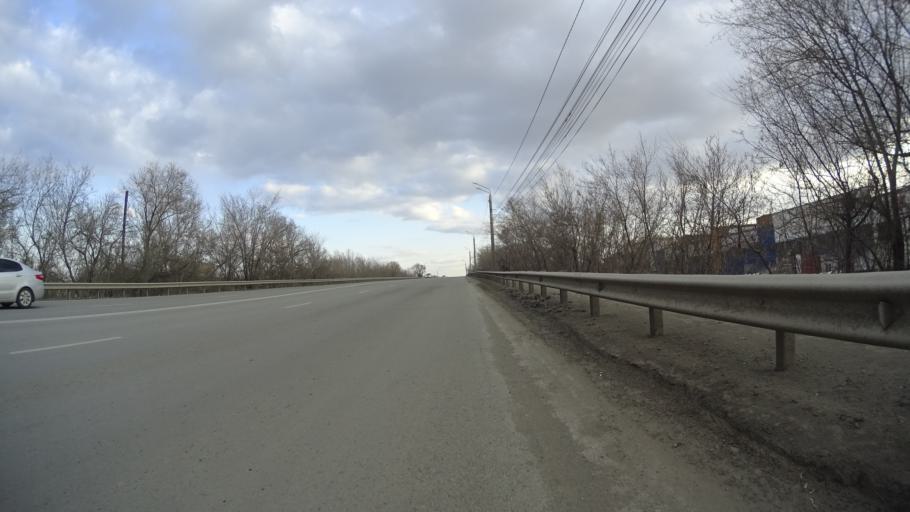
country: RU
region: Chelyabinsk
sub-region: Gorod Chelyabinsk
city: Chelyabinsk
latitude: 55.1044
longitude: 61.3873
